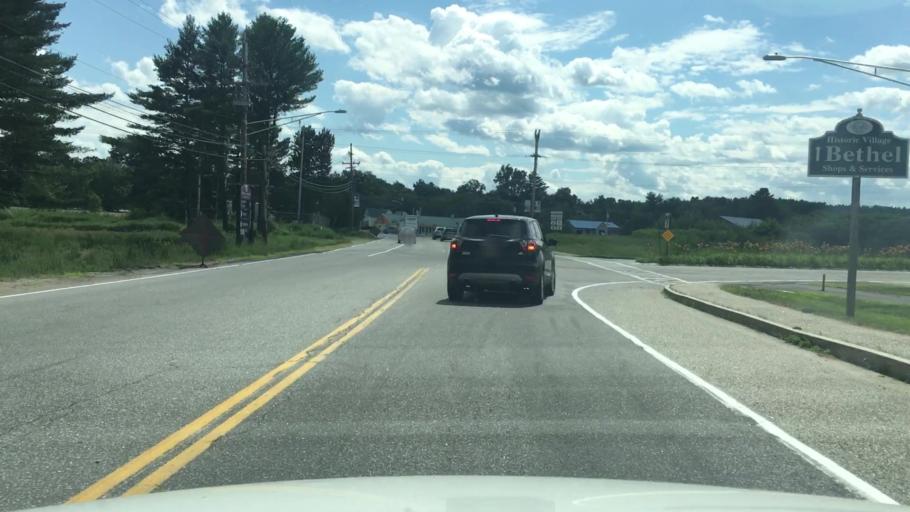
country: US
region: Maine
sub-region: Oxford County
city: Bethel
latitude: 44.4136
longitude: -70.7869
